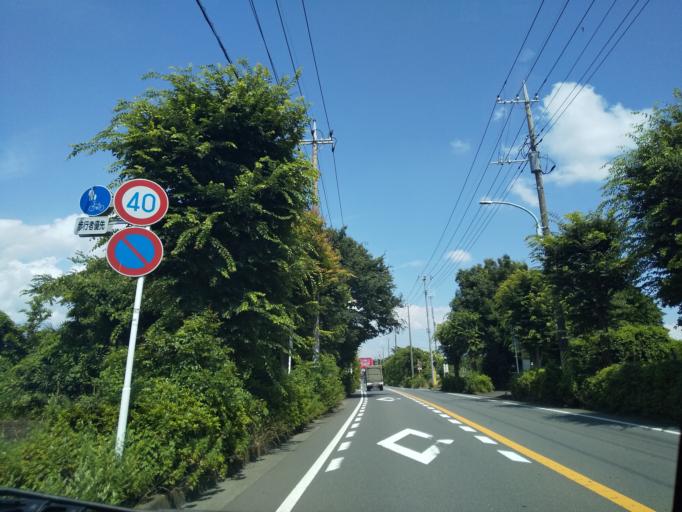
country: JP
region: Kanagawa
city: Zama
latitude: 35.4900
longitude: 139.4181
